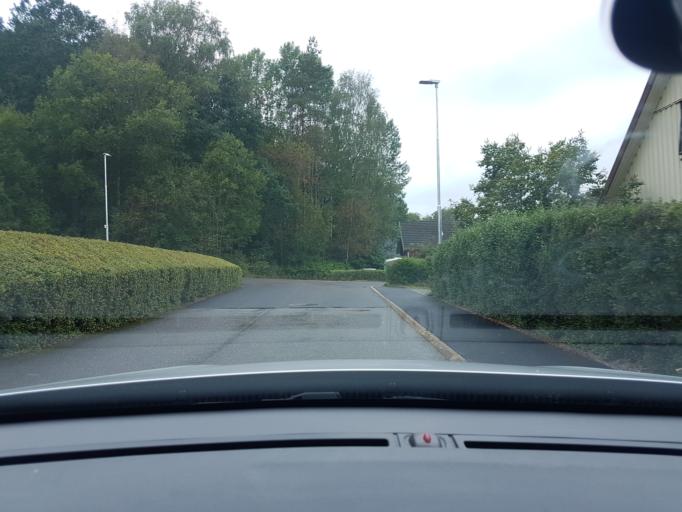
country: SE
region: Vaestra Goetaland
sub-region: Ale Kommun
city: Salanda
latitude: 57.9816
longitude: 12.2184
